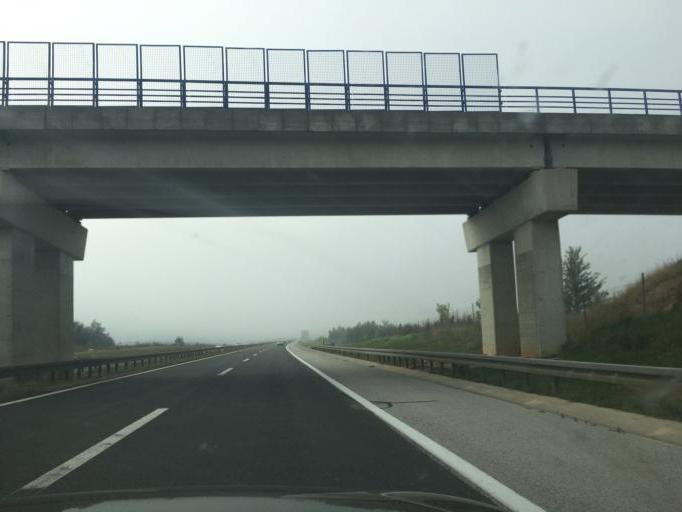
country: HR
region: Licko-Senjska
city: Gospic
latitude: 44.5904
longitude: 15.4350
